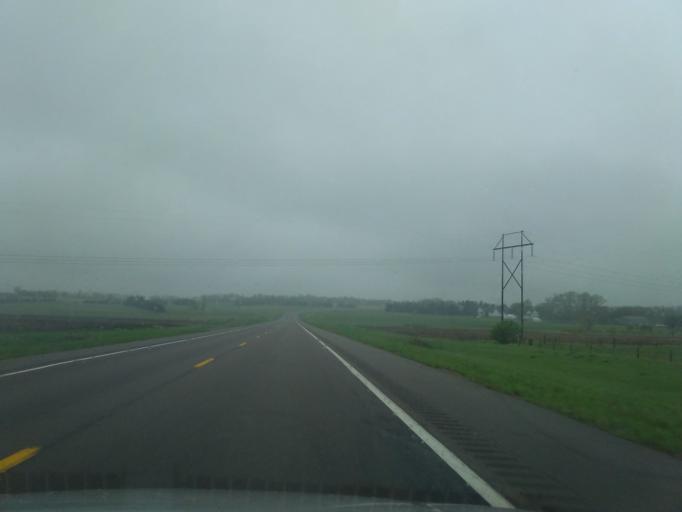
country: US
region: Nebraska
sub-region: Madison County
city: Norfolk
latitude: 42.0846
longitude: -97.3240
